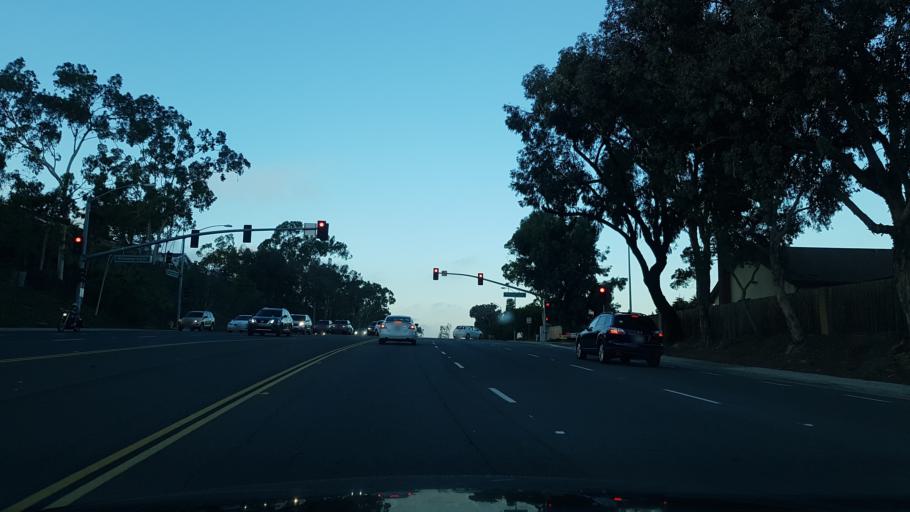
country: US
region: California
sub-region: San Diego County
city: Encinitas
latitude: 33.0396
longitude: -117.2594
